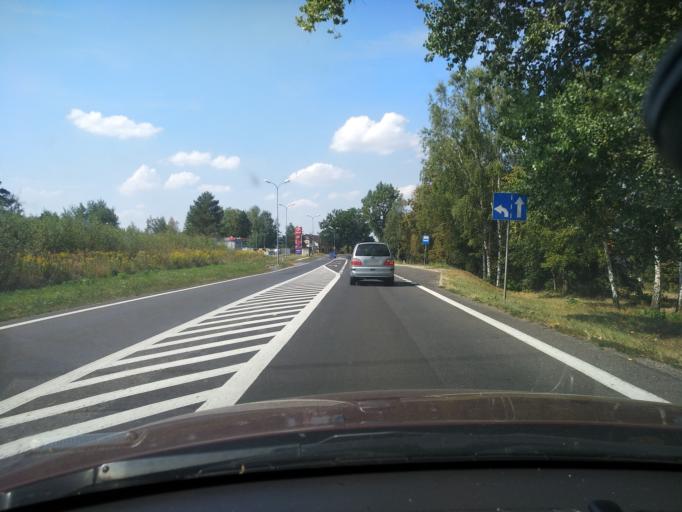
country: PL
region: Lower Silesian Voivodeship
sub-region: Powiat lubanski
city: Luban
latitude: 51.0988
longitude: 15.3109
